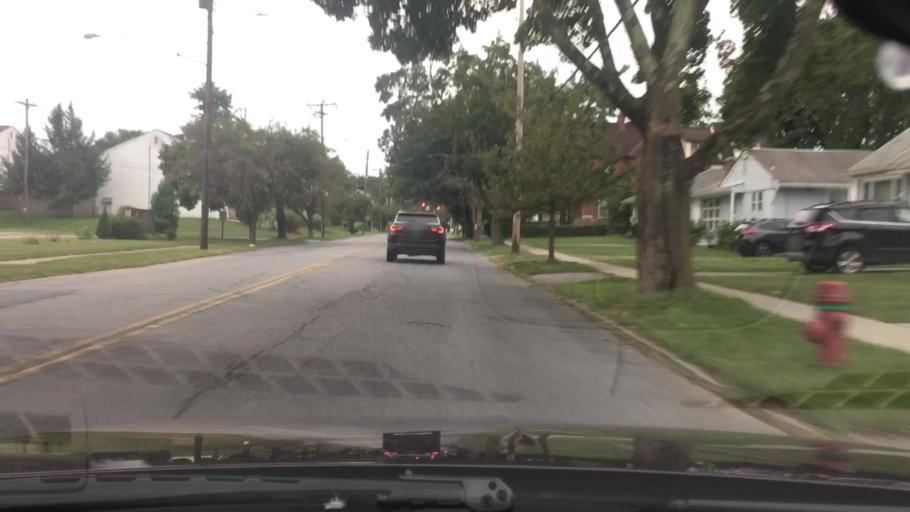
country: US
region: New York
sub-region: Dutchess County
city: Arlington
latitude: 41.6876
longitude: -73.9091
